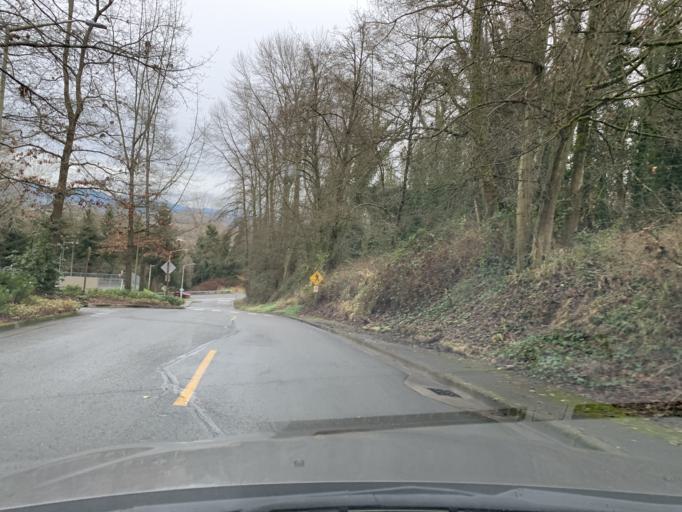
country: US
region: Washington
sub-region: King County
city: Tukwila
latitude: 47.4599
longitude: -122.2699
